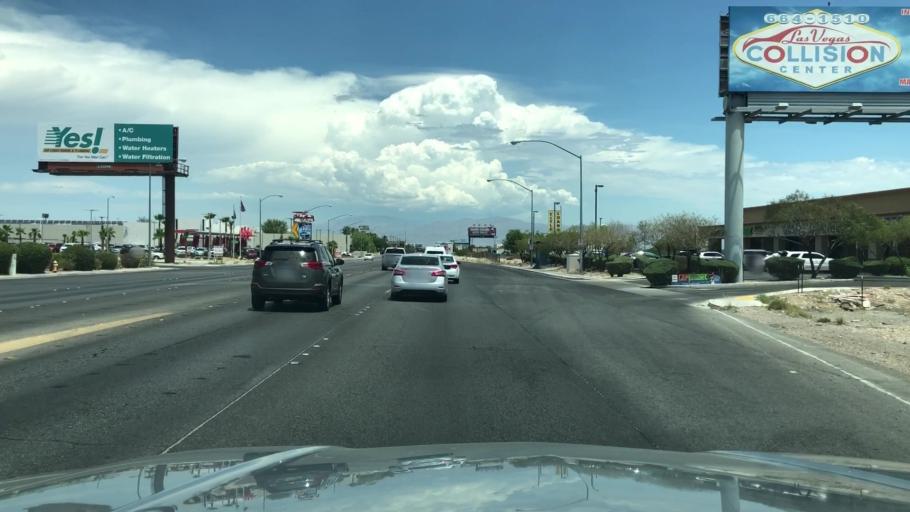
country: US
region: Nevada
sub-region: Clark County
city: Spring Valley
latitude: 36.0760
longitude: -115.2078
